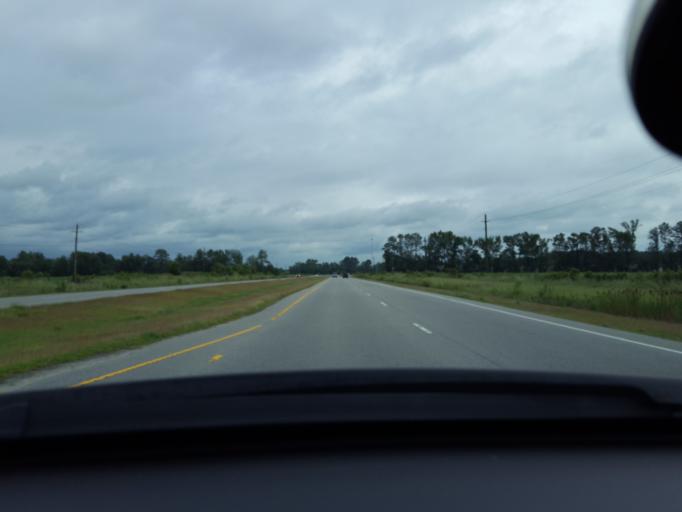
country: US
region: North Carolina
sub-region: Pitt County
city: Ayden
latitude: 35.4580
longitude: -77.4329
